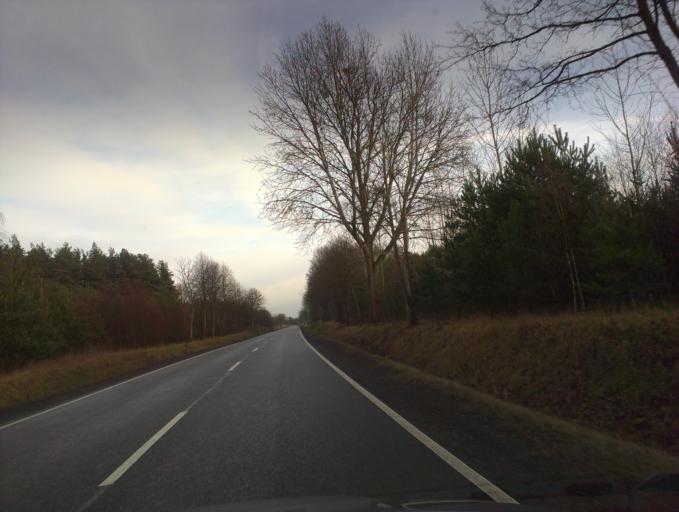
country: PL
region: West Pomeranian Voivodeship
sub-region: Powiat szczecinecki
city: Szczecinek
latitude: 53.7350
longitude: 16.7804
